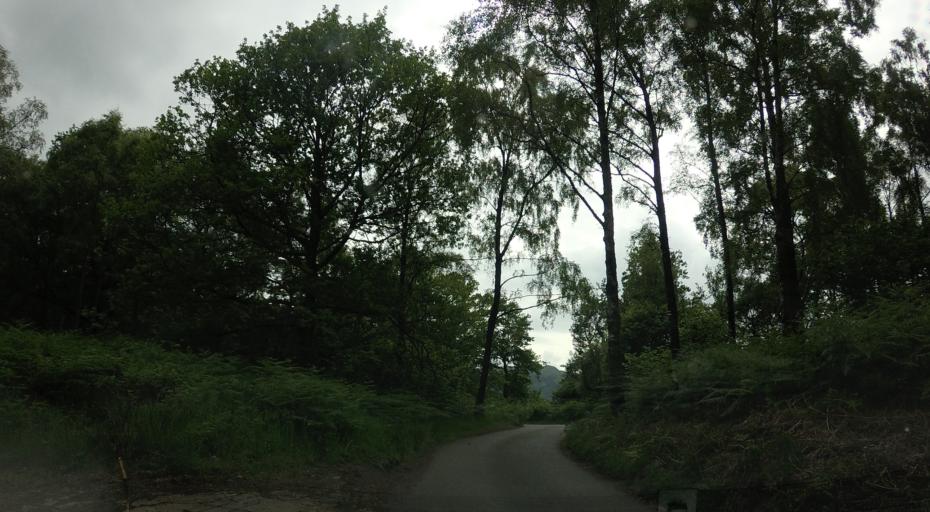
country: GB
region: England
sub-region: Cumbria
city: Keswick
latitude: 54.5614
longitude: -3.1323
